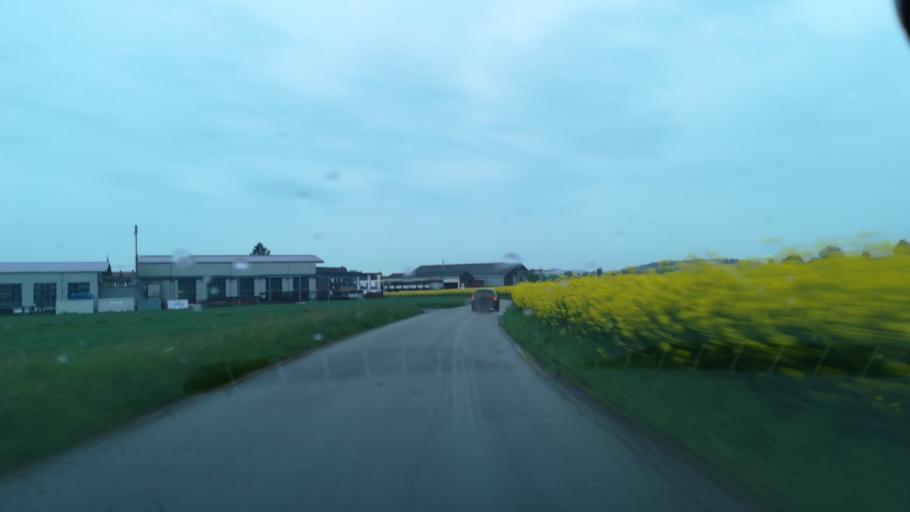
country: CH
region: Zurich
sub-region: Bezirk Buelach
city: End-Hoeri
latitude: 47.5120
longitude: 8.5021
